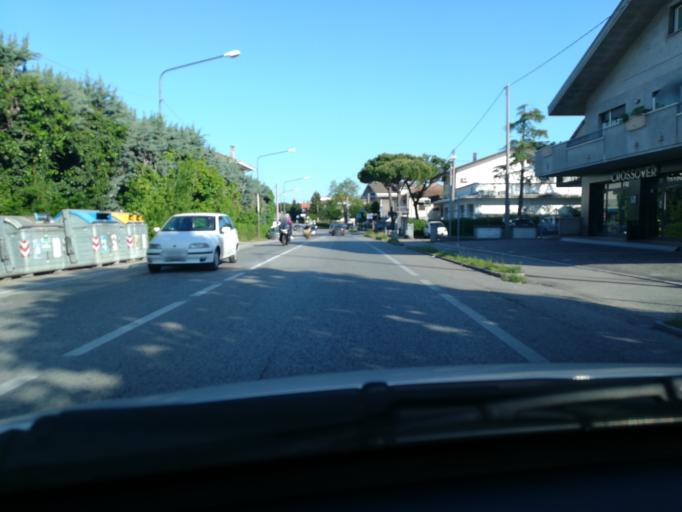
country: IT
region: Emilia-Romagna
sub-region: Provincia di Rimini
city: Riccione
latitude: 43.9911
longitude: 12.6655
